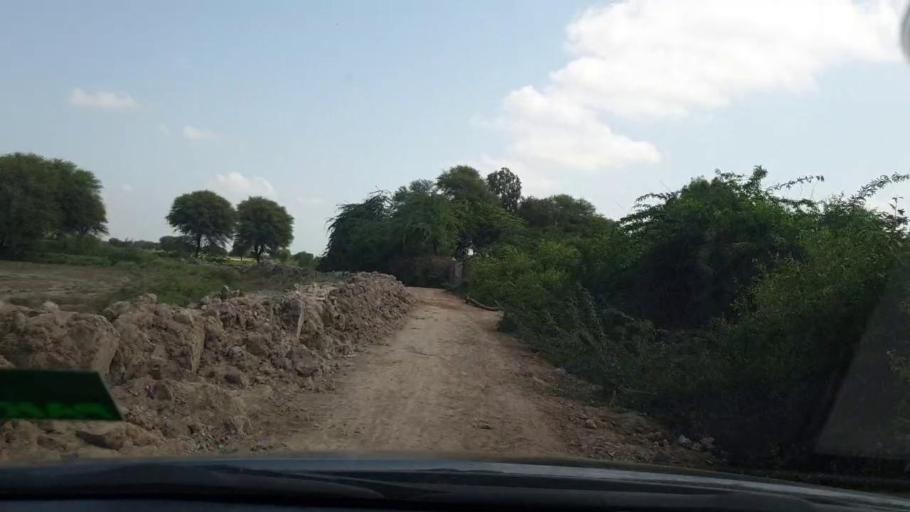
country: PK
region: Sindh
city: Tando Bago
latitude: 24.9572
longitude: 69.0765
